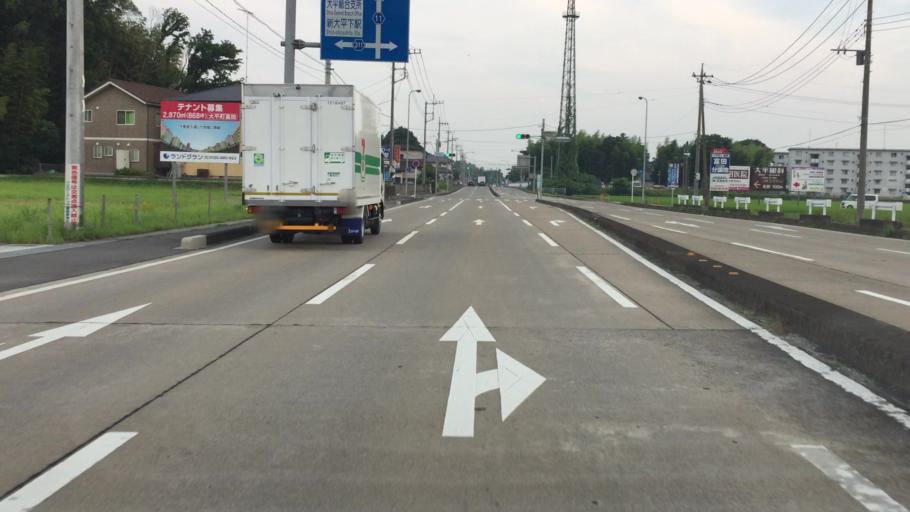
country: JP
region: Tochigi
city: Tochigi
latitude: 36.3396
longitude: 139.6958
